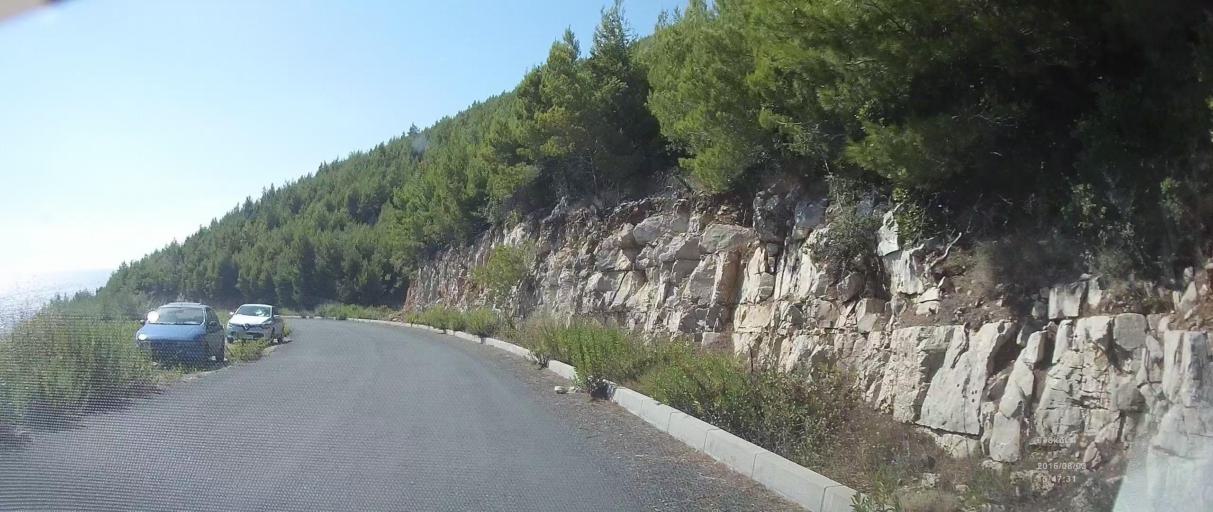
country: HR
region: Dubrovacko-Neretvanska
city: Blato
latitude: 42.7355
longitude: 17.5083
